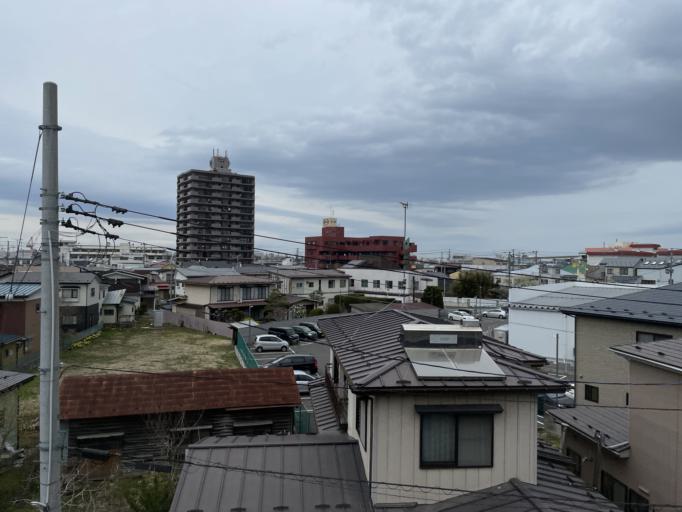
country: JP
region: Aomori
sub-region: Hachinohe Shi
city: Uchimaru
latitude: 40.5188
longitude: 141.5123
